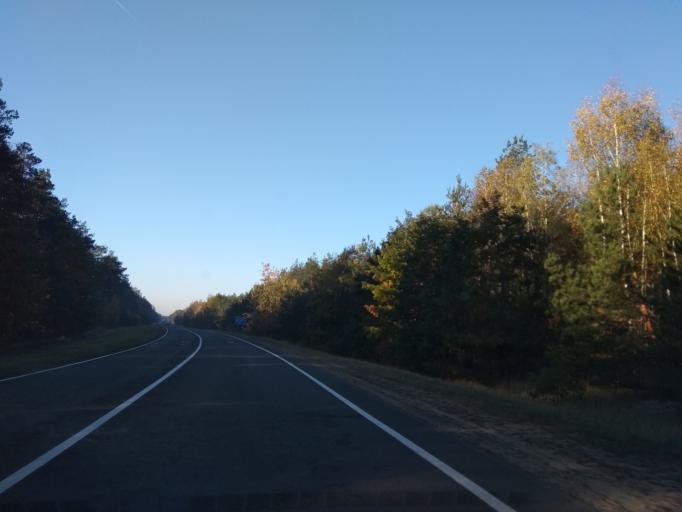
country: BY
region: Brest
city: Kobryn
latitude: 52.0251
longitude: 24.2491
